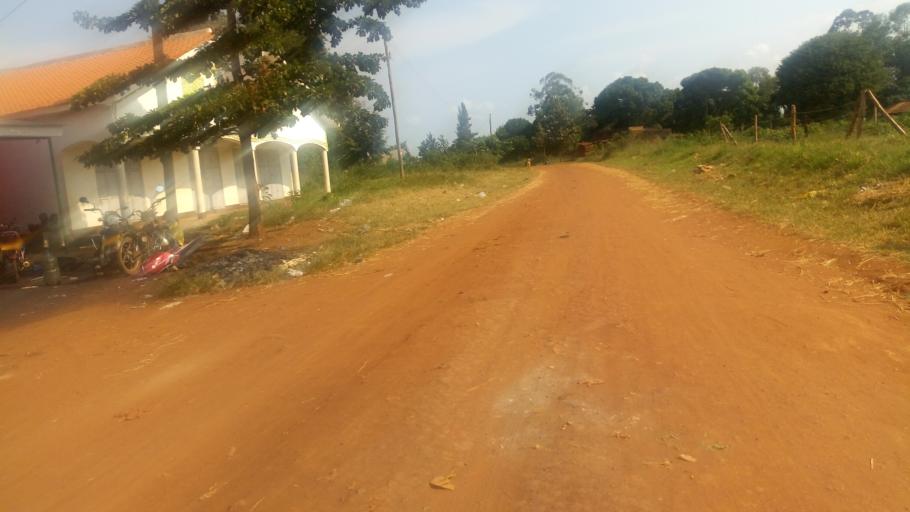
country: UG
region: Western Region
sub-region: Kiryandongo District
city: Kiryandongo
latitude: 1.8087
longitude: 32.0080
